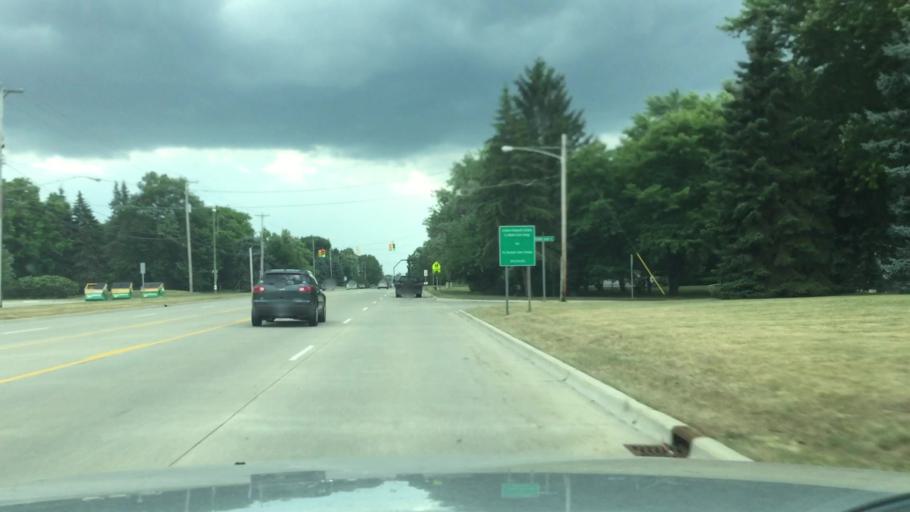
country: US
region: Michigan
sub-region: Genesee County
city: Flushing
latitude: 43.0253
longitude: -83.7734
